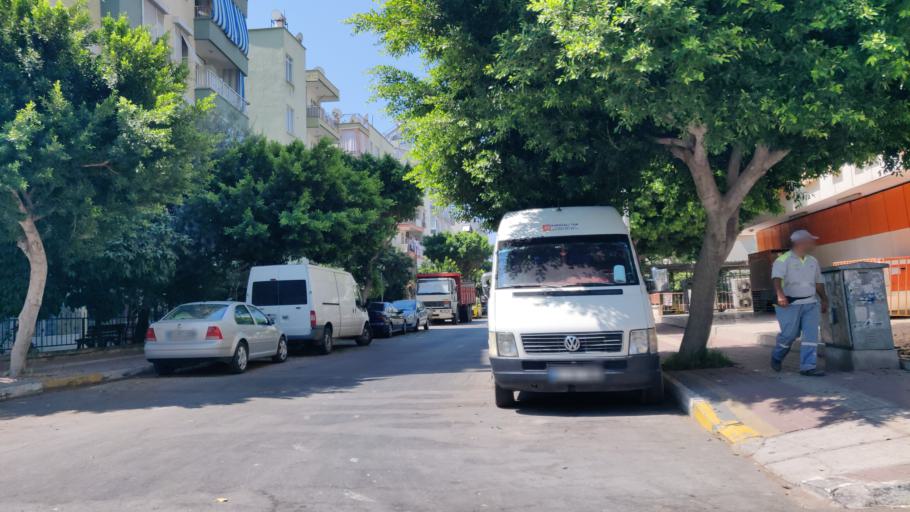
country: TR
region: Antalya
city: Antalya
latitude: 36.9092
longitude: 30.6832
